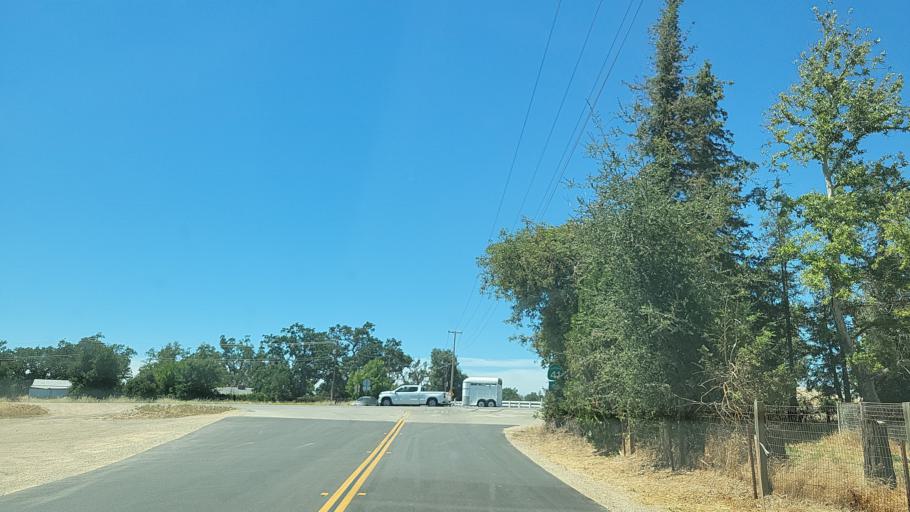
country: US
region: California
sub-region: San Luis Obispo County
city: Atascadero
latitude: 35.5040
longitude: -120.6520
